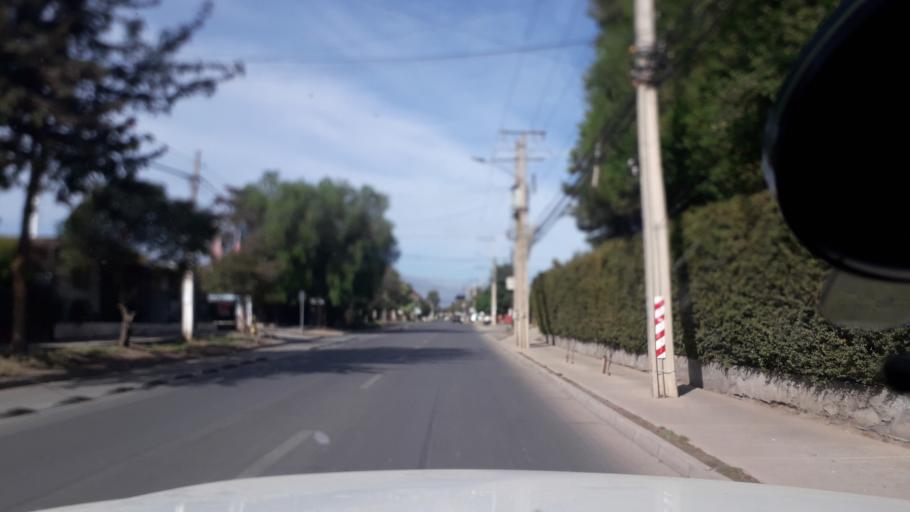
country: CL
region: Valparaiso
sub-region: Provincia de San Felipe
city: San Felipe
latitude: -32.7530
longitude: -70.7137
